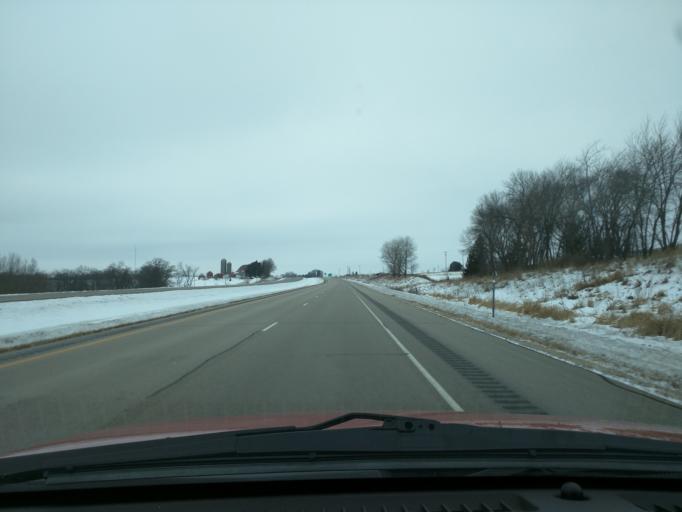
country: US
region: Wisconsin
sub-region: Trempealeau County
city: Trempealeau
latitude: 43.9116
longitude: -91.5651
